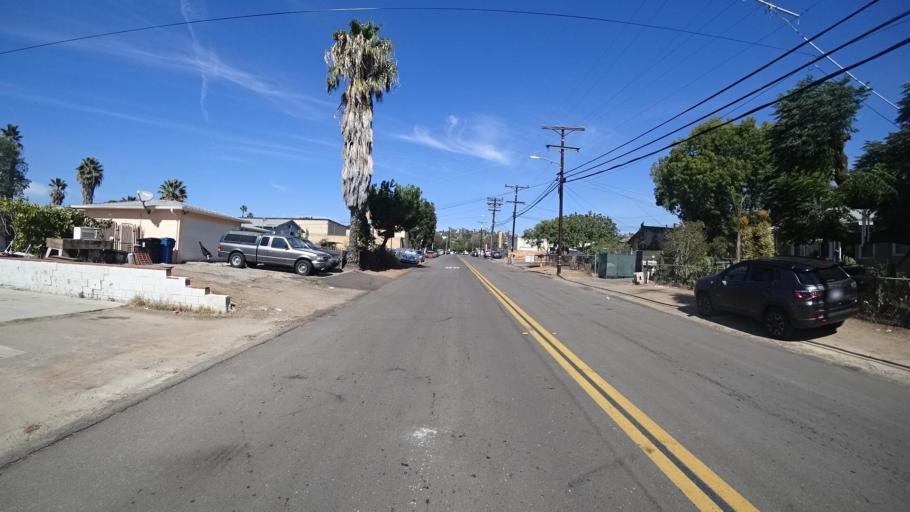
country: US
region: California
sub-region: San Diego County
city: La Presa
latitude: 32.7135
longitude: -117.0075
